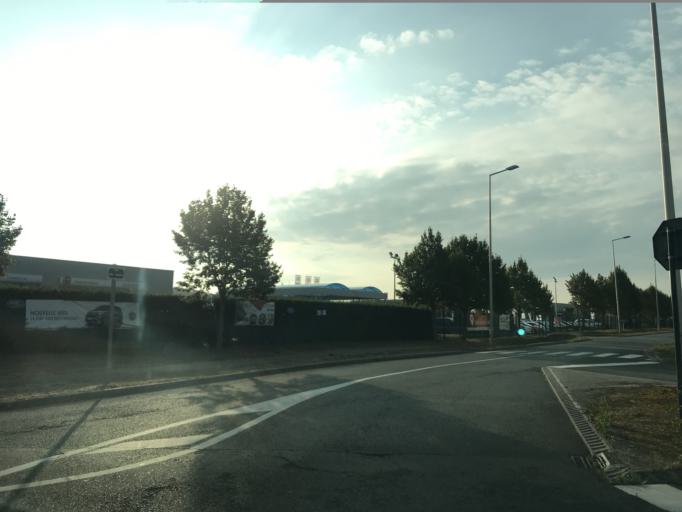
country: FR
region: Haute-Normandie
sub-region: Departement de l'Eure
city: Gravigny
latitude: 49.0261
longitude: 1.1876
